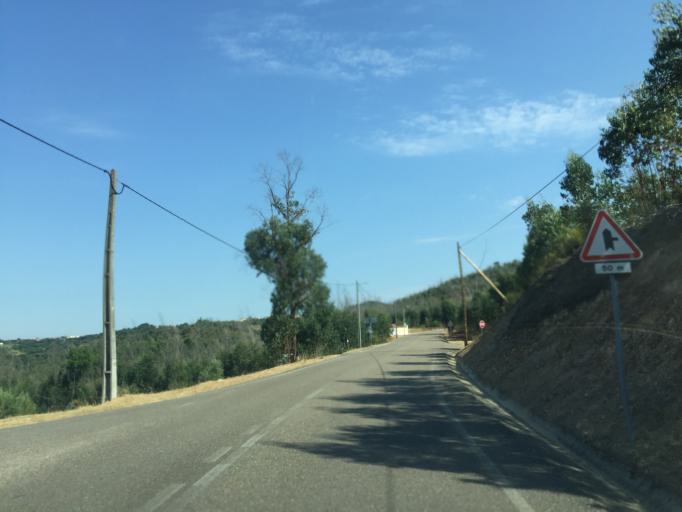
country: PT
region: Santarem
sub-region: Tomar
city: Tomar
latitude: 39.5781
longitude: -8.2973
